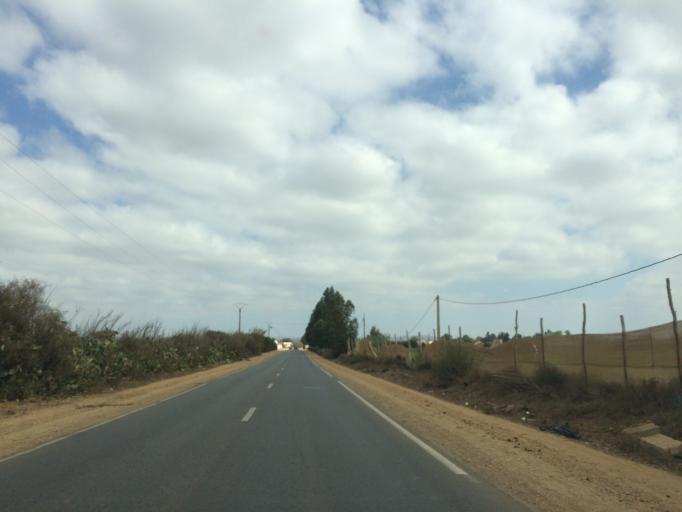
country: MA
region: Gharb-Chrarda-Beni Hssen
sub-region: Kenitra Province
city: Lalla Mimouna
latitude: 34.8429
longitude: -6.1665
